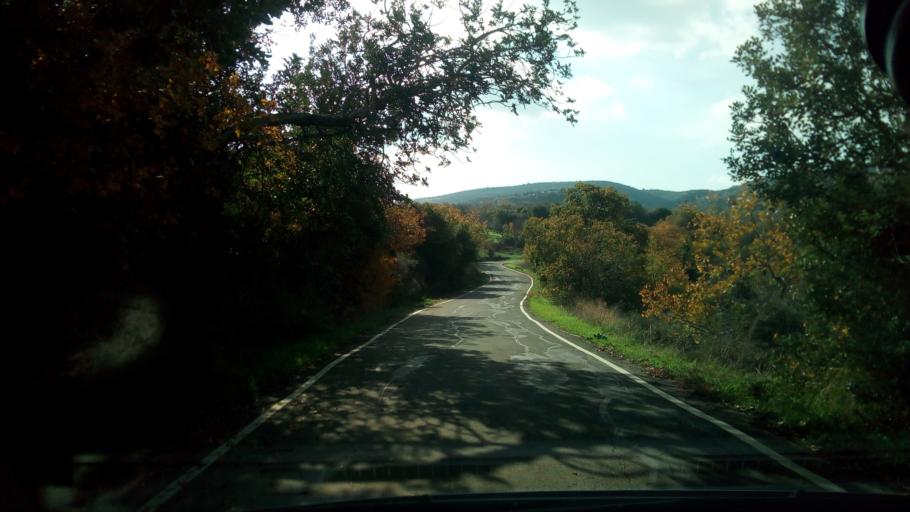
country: CY
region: Pafos
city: Polis
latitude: 34.9586
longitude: 32.4313
